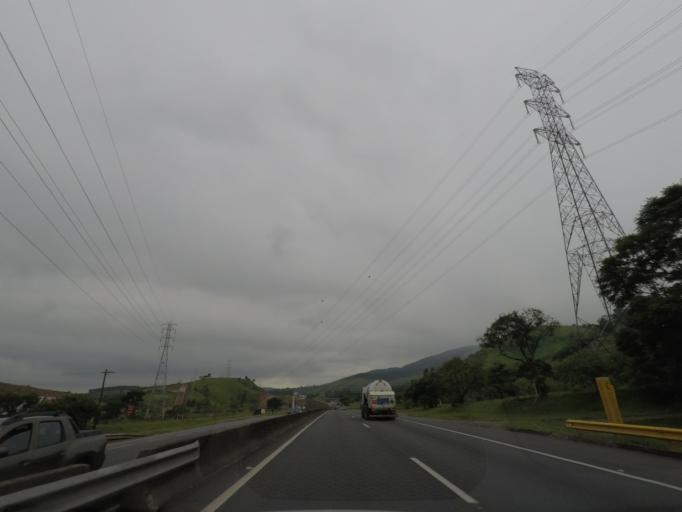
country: BR
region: Sao Paulo
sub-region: Aparecida
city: Aparecida
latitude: -22.8757
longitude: -45.2670
